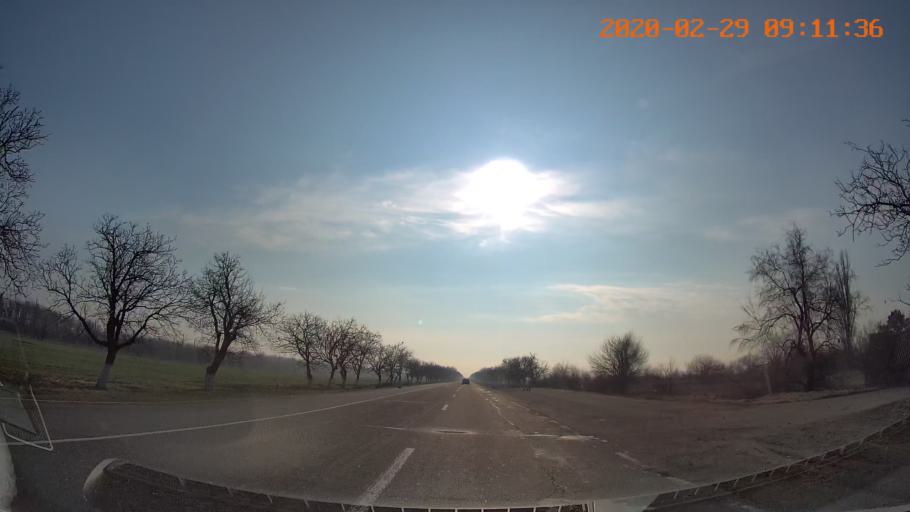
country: MD
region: Telenesti
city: Slobozia
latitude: 46.8337
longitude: 29.8028
